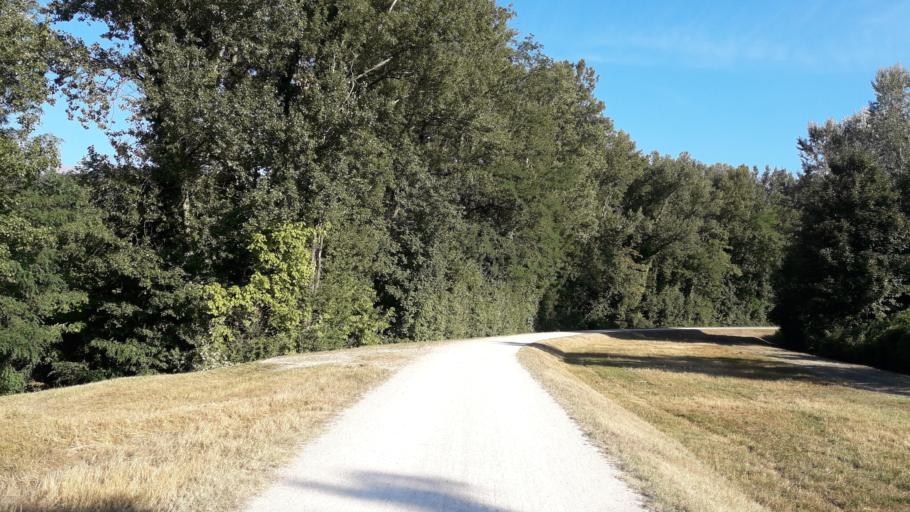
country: FR
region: Rhone-Alpes
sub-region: Departement de l'Isere
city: Gieres
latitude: 45.2008
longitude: 5.7979
